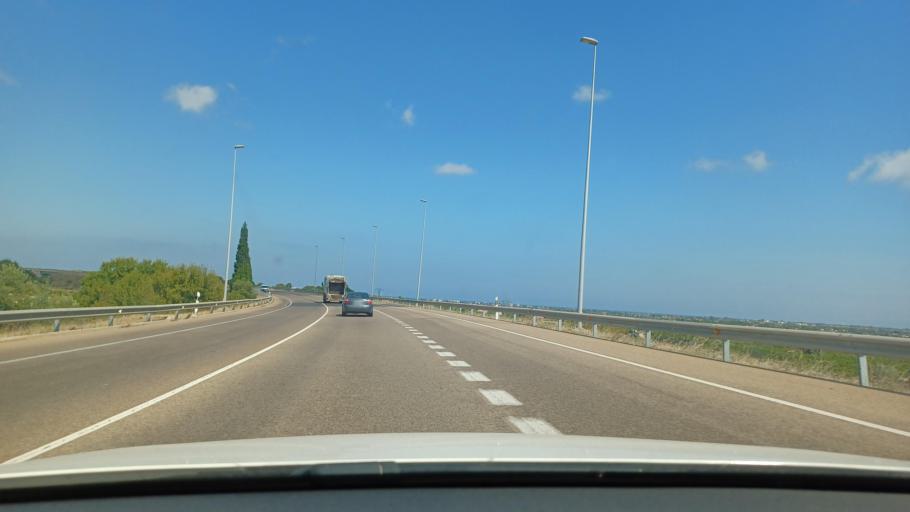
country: ES
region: Valencia
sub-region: Provincia de Castello
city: Castello de la Plana
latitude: 40.0239
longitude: -0.0159
